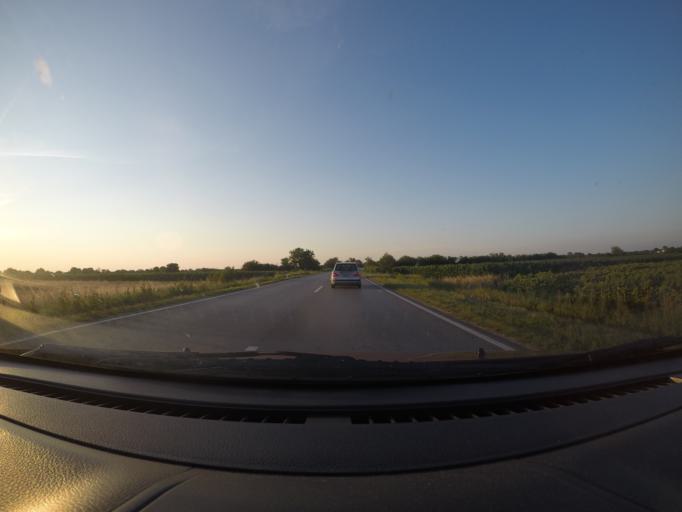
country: RS
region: Central Serbia
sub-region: Branicevski Okrug
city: Pozarevac
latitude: 44.6299
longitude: 21.1446
